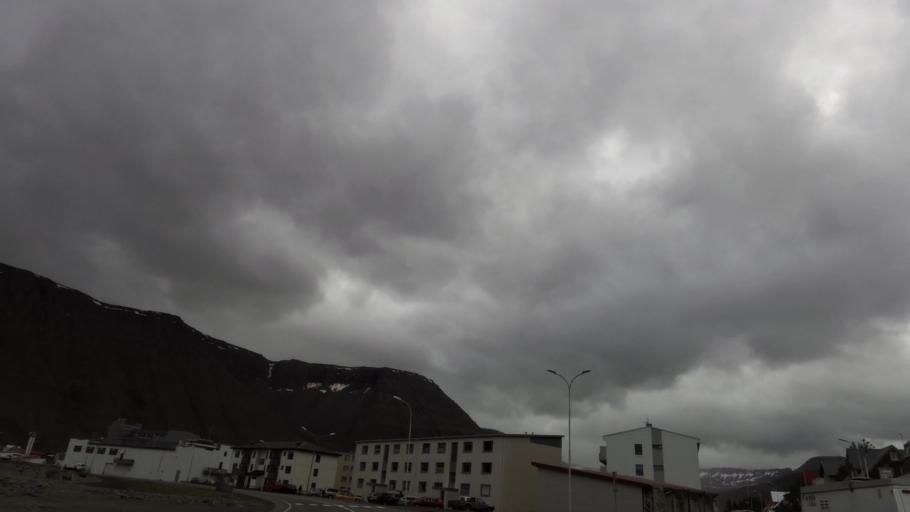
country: IS
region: Westfjords
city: Isafjoerdur
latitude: 66.0783
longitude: -23.1256
